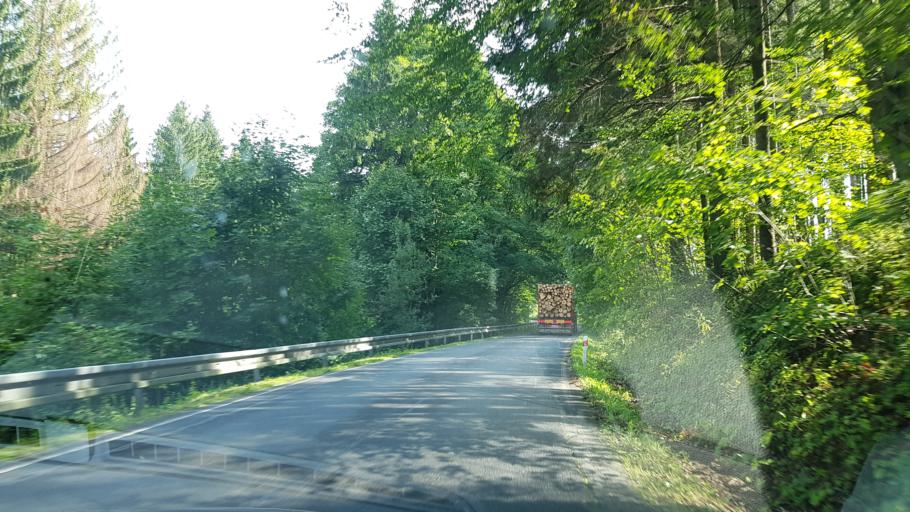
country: CZ
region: Olomoucky
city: Zlate Hory
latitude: 50.2479
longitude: 17.3602
